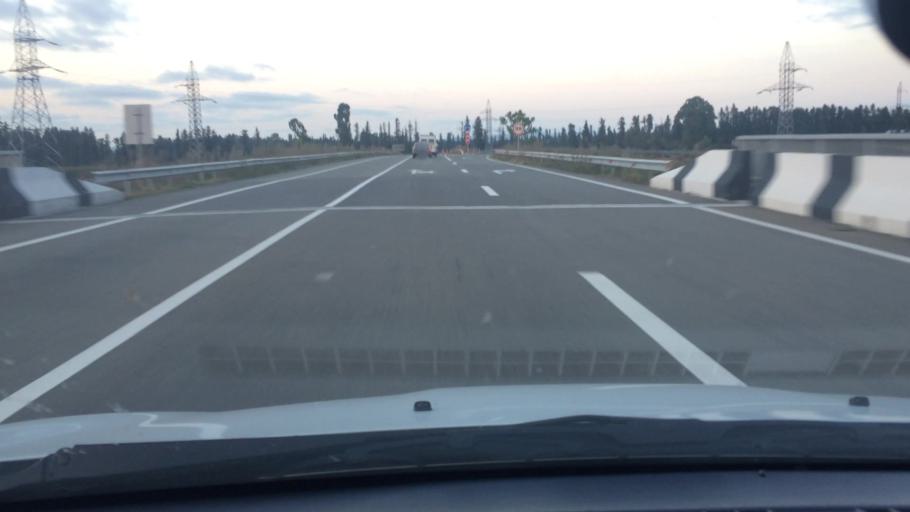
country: GE
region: Ajaria
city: Ochkhamuri
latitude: 41.8312
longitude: 41.8212
